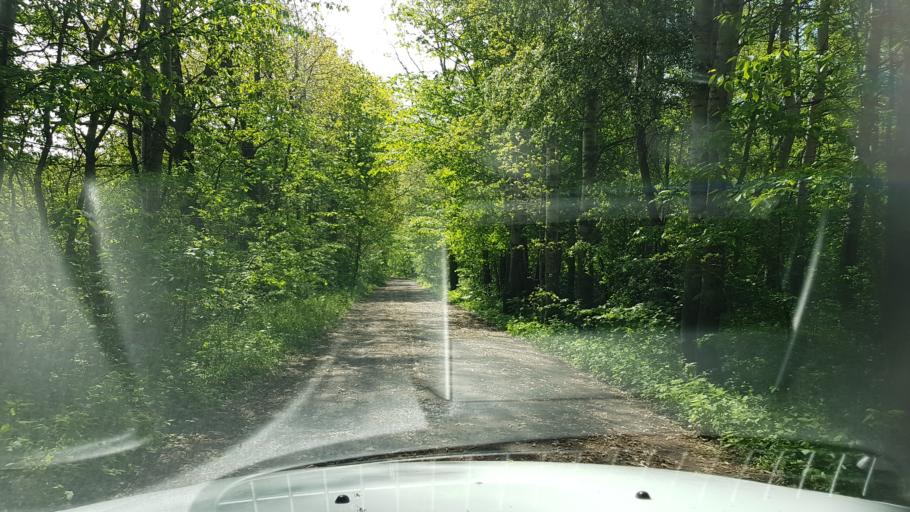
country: PL
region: West Pomeranian Voivodeship
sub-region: Powiat kolobrzeski
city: Ustronie Morskie
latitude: 54.2265
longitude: 15.8084
